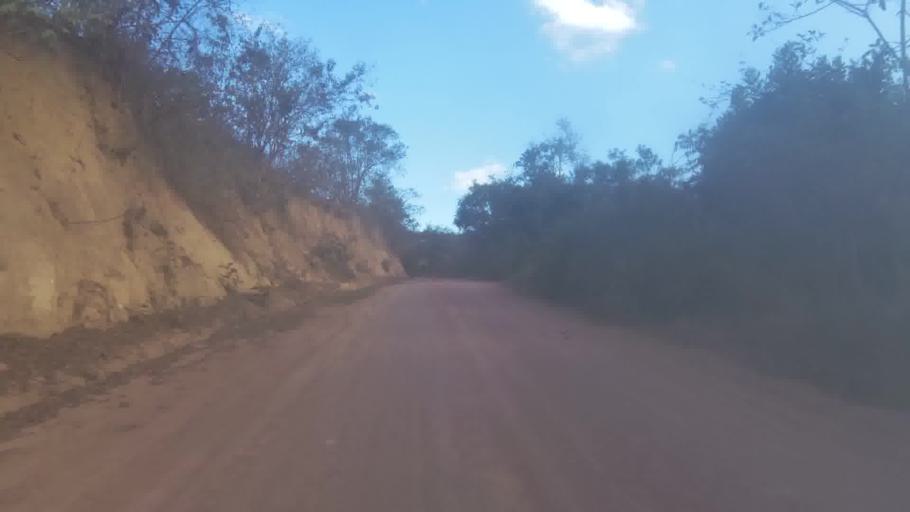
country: BR
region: Espirito Santo
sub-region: Mimoso Do Sul
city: Mimoso do Sul
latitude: -21.0853
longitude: -41.1457
